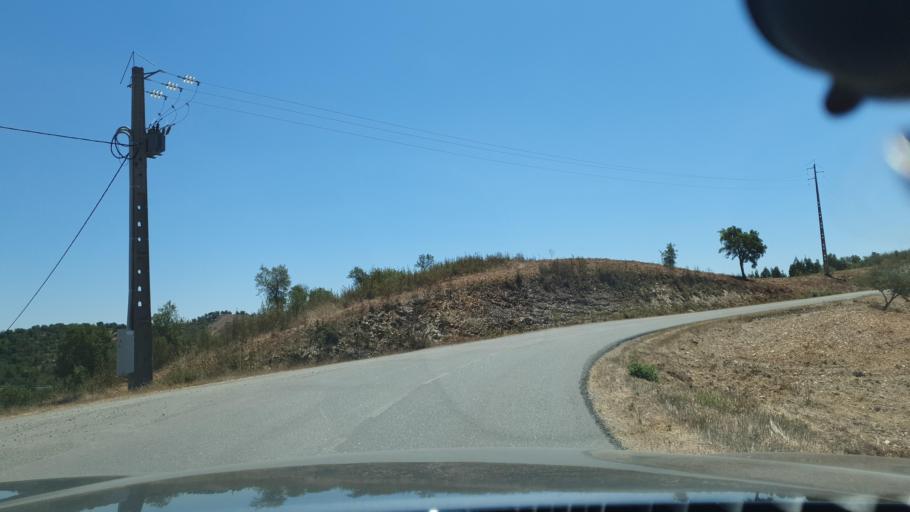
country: PT
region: Beja
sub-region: Odemira
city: Odemira
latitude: 37.5526
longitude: -8.4393
